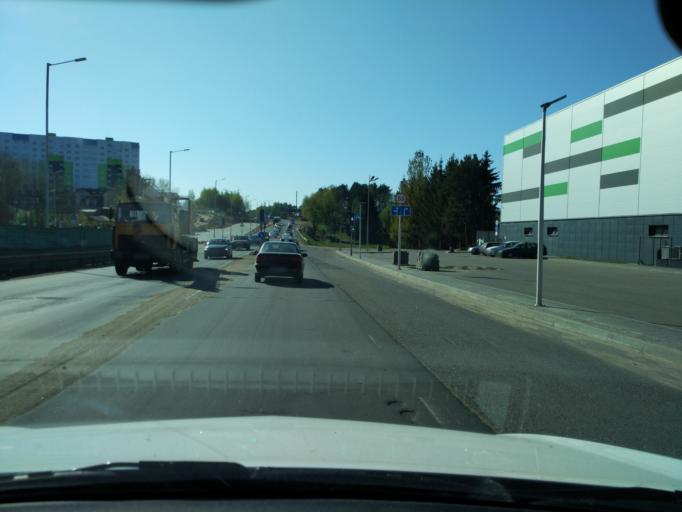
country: BY
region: Minsk
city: Borovlyany
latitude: 53.9641
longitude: 27.6733
